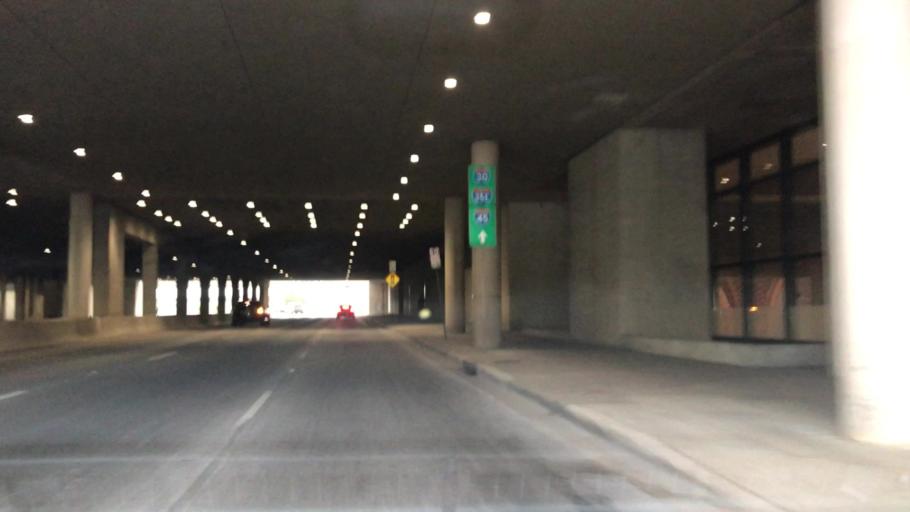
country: US
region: Texas
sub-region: Dallas County
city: Dallas
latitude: 32.7747
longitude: -96.8017
